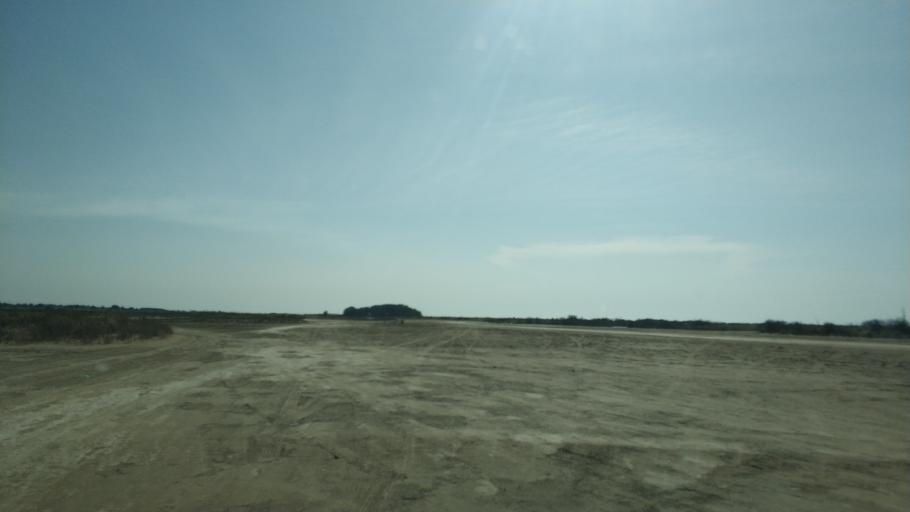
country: AL
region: Fier
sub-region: Rrethi i Lushnjes
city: Divjake
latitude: 40.9617
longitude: 19.4736
